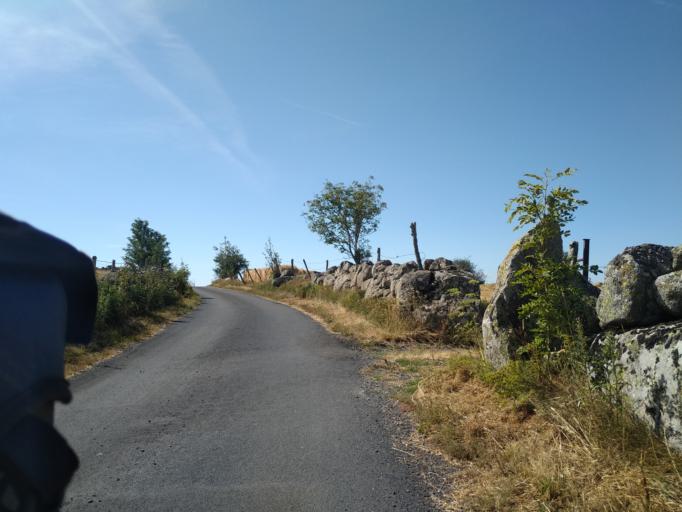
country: FR
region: Languedoc-Roussillon
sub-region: Departement de la Lozere
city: Aumont-Aubrac
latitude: 44.6704
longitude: 3.1023
